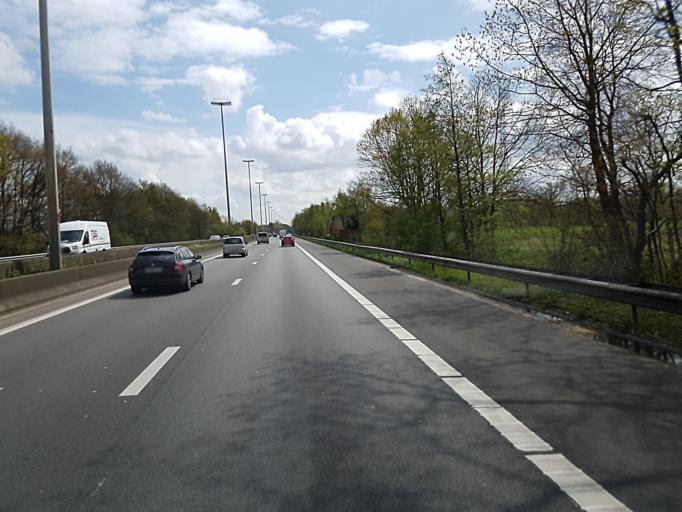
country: BE
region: Flanders
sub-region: Provincie Limburg
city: Hasselt
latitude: 50.9581
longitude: 5.2684
